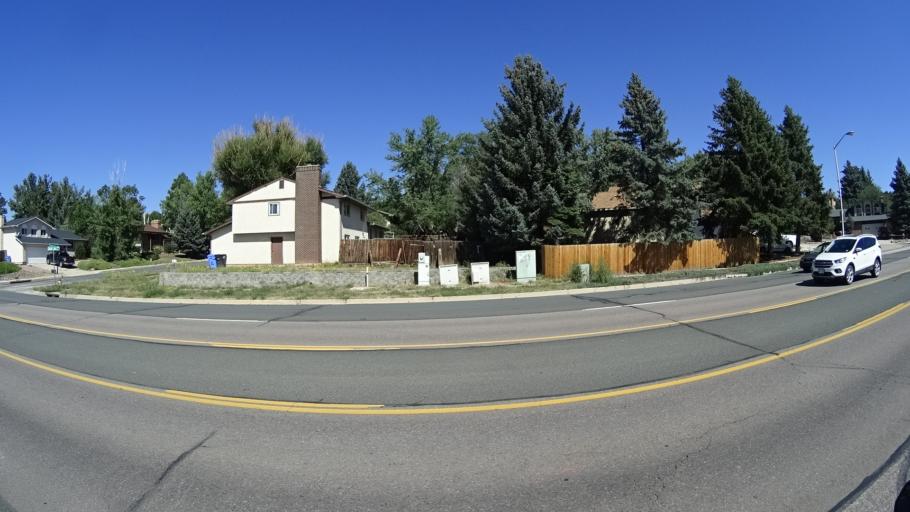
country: US
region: Colorado
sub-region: El Paso County
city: Cimarron Hills
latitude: 38.8681
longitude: -104.7267
